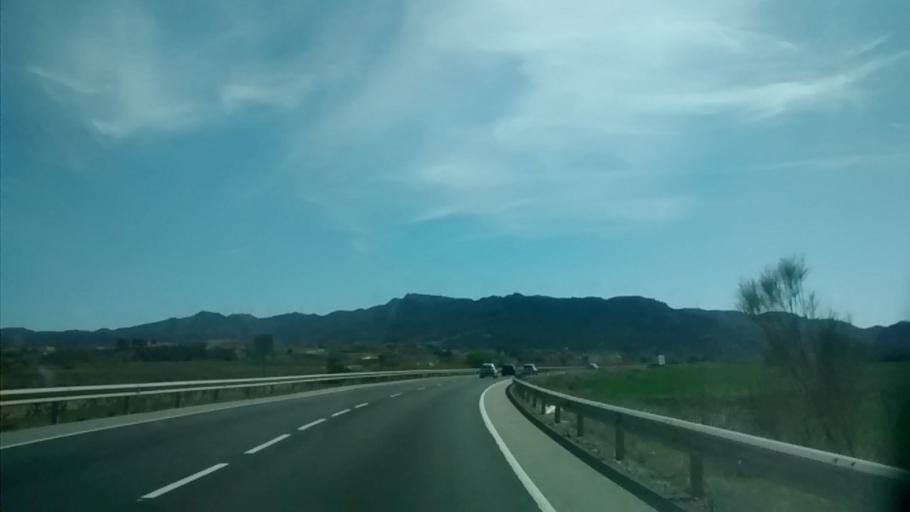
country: ES
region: Catalonia
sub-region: Provincia de Tarragona
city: Asco
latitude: 41.1872
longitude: 0.5751
